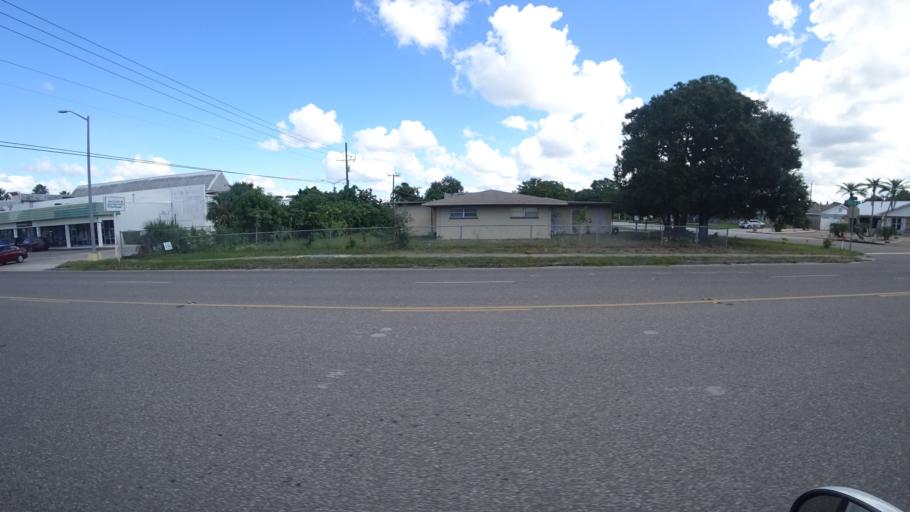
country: US
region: Florida
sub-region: Manatee County
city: West Bradenton
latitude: 27.4942
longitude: -82.6205
